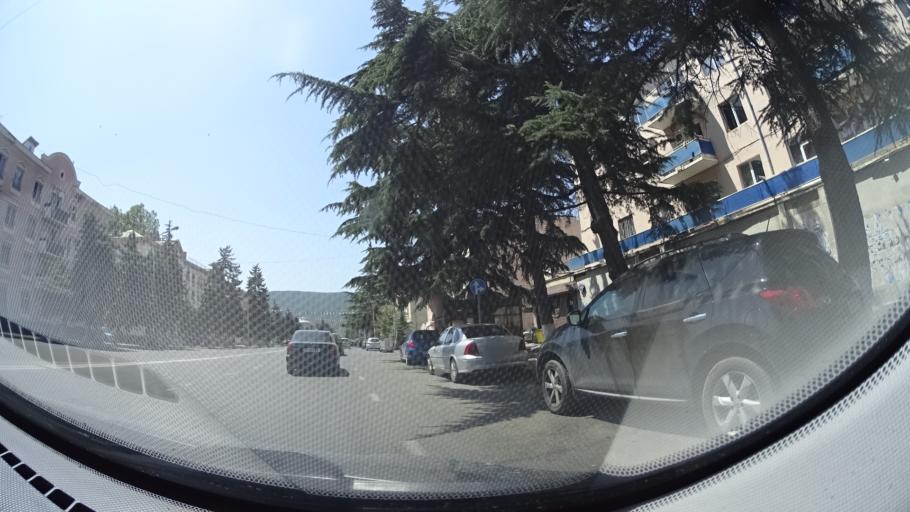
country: GE
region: Shida Kartli
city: Gori
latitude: 41.9843
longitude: 44.1129
